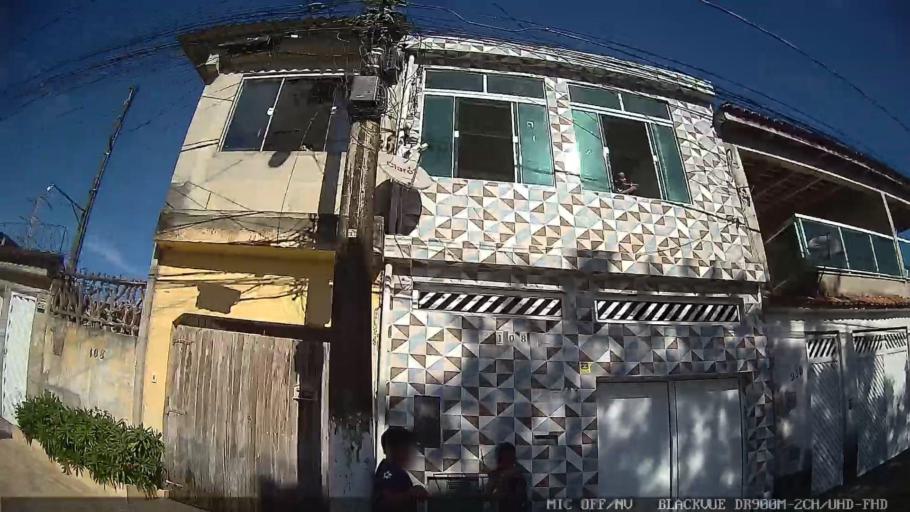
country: BR
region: Sao Paulo
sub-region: Santos
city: Santos
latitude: -23.9327
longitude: -46.2889
